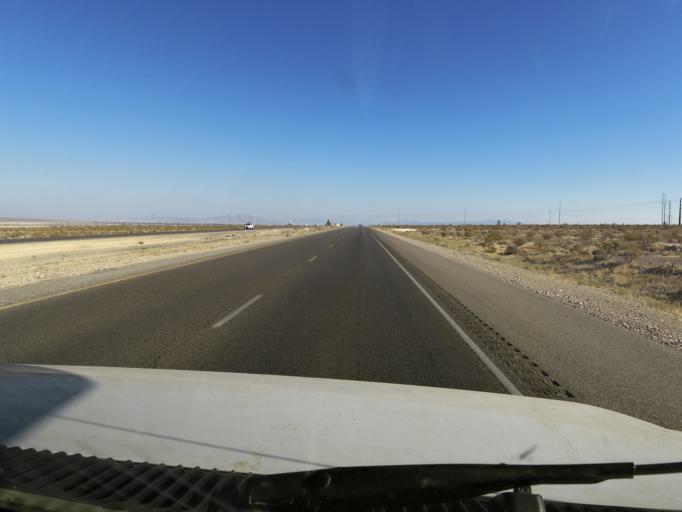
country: US
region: Nevada
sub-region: Clark County
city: Summerlin South
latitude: 36.3446
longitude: -115.3306
